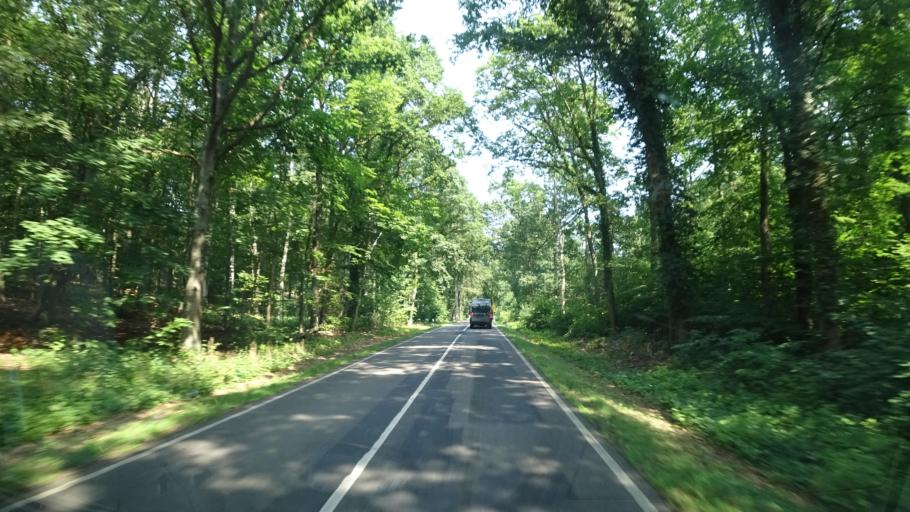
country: DE
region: Mecklenburg-Vorpommern
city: Seebad Heringsdorf
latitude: 53.8885
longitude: 14.1760
